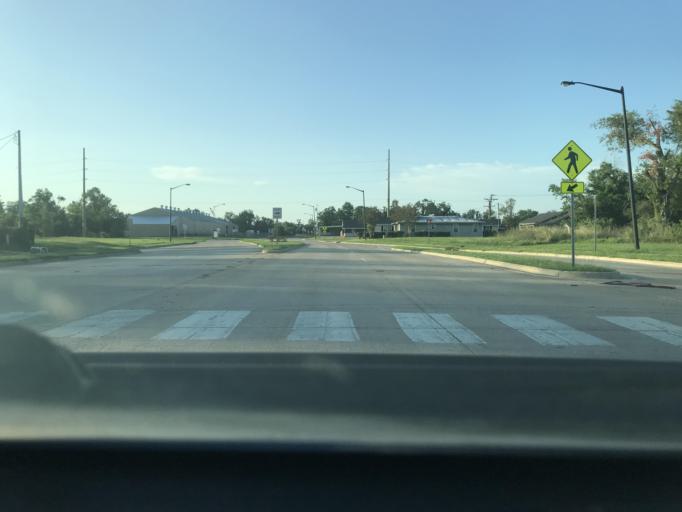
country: US
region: Louisiana
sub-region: Calcasieu Parish
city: Lake Charles
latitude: 30.2409
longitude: -93.2043
